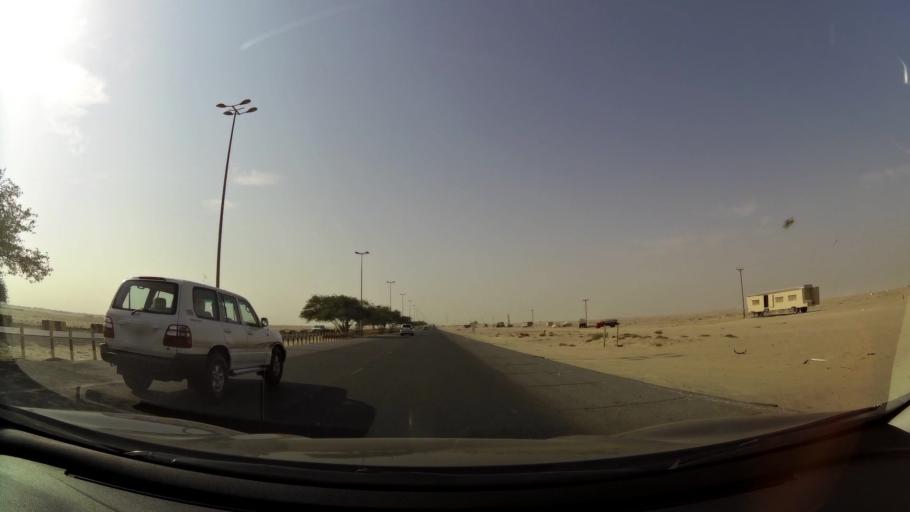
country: KW
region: Al Ahmadi
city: Al Ahmadi
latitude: 28.9215
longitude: 48.1020
